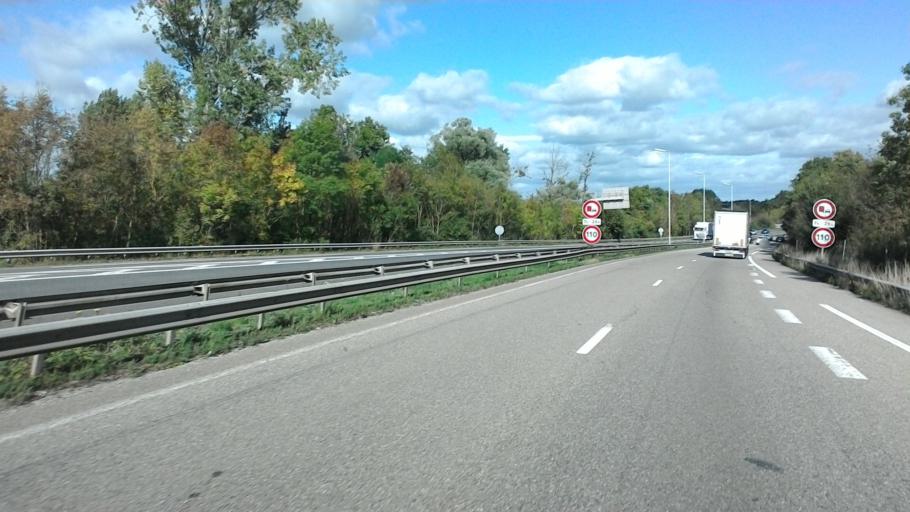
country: FR
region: Lorraine
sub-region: Departement de Meurthe-et-Moselle
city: Dommartin-les-Toul
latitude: 48.6772
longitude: 5.9235
